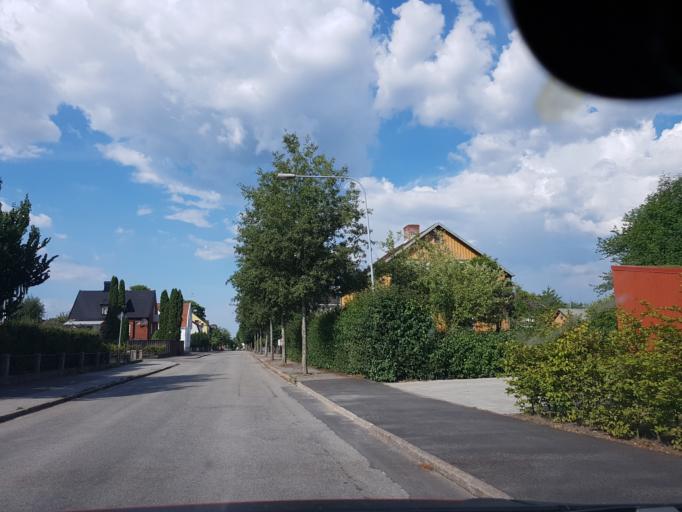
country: SE
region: Joenkoeping
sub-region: Gislaveds Kommun
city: Gislaved
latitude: 57.2992
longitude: 13.5376
